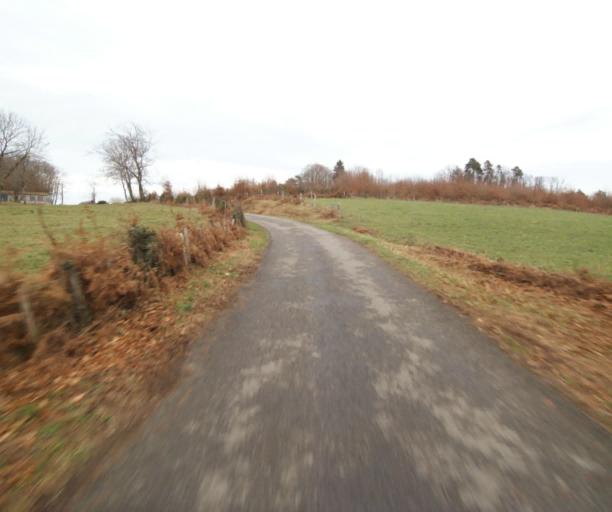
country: FR
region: Limousin
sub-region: Departement de la Correze
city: Chameyrat
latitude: 45.2313
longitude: 1.6867
